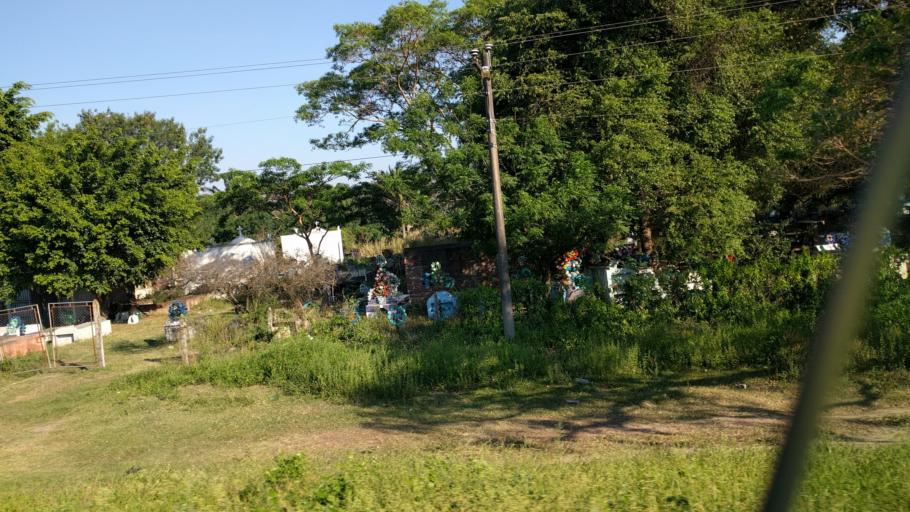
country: BO
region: Santa Cruz
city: Jorochito
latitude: -18.1505
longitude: -63.4898
